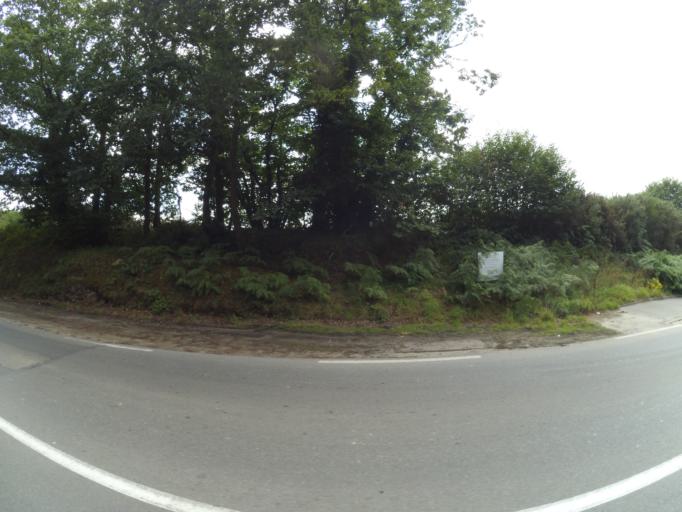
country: FR
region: Brittany
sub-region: Departement du Finistere
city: Ergue-Gaberic
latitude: 47.9810
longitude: -4.0256
